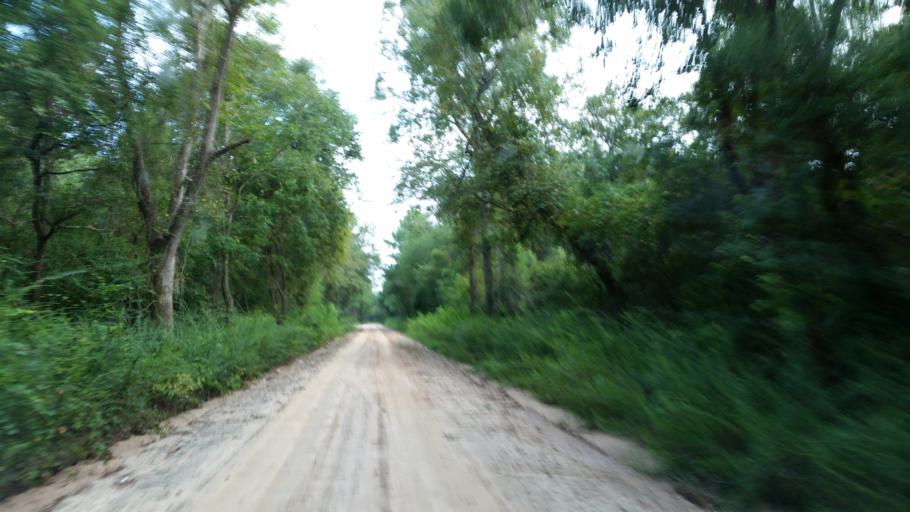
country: US
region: Georgia
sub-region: Lowndes County
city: Hahira
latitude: 31.0377
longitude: -83.3942
